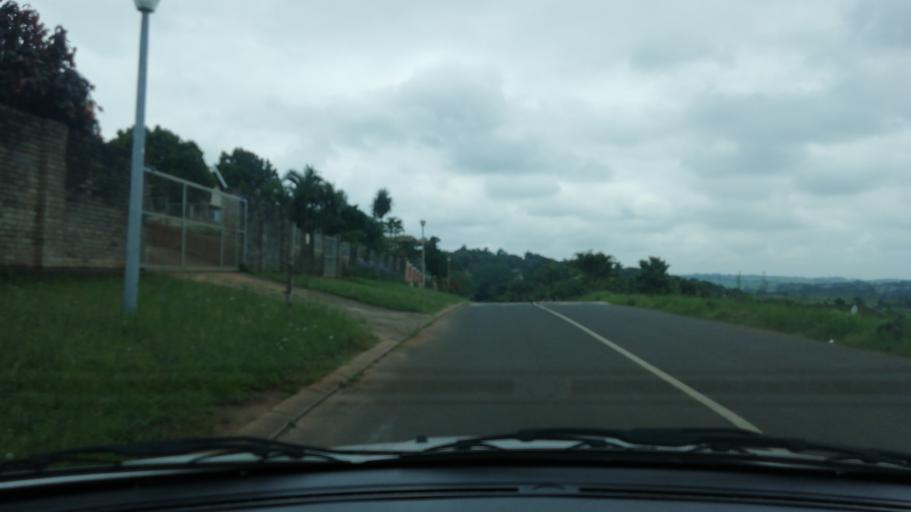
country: ZA
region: KwaZulu-Natal
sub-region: uThungulu District Municipality
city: Empangeni
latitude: -28.7621
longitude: 31.8854
